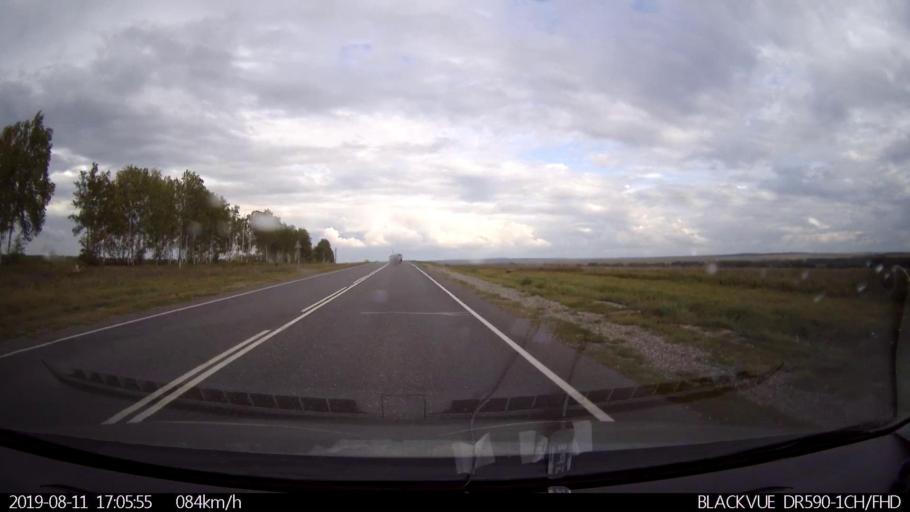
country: RU
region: Ulyanovsk
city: Mayna
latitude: 54.2962
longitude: 47.7956
